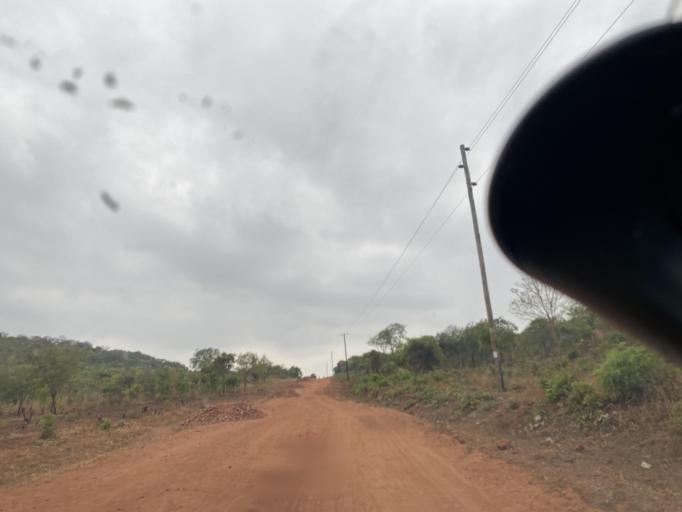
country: ZM
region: Lusaka
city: Chongwe
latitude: -15.1765
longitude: 28.7635
